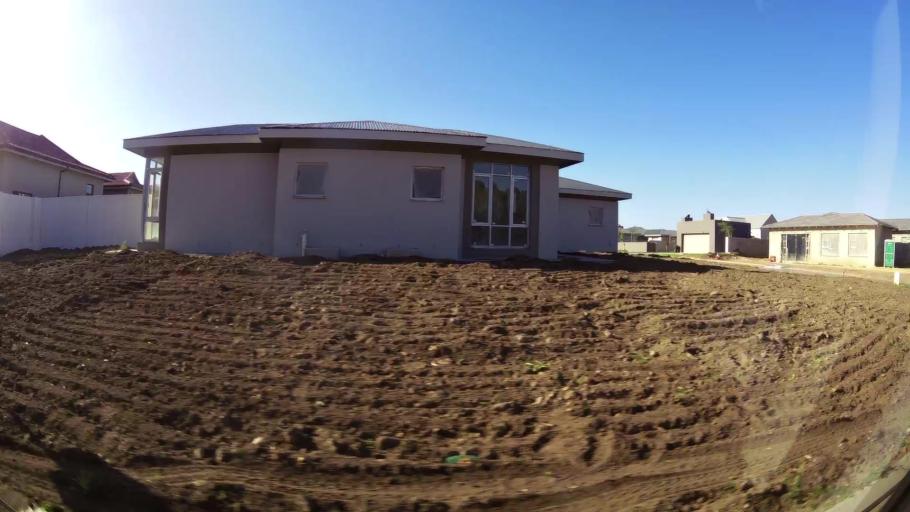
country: ZA
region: Western Cape
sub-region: Eden District Municipality
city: George
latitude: -33.9606
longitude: 22.4192
